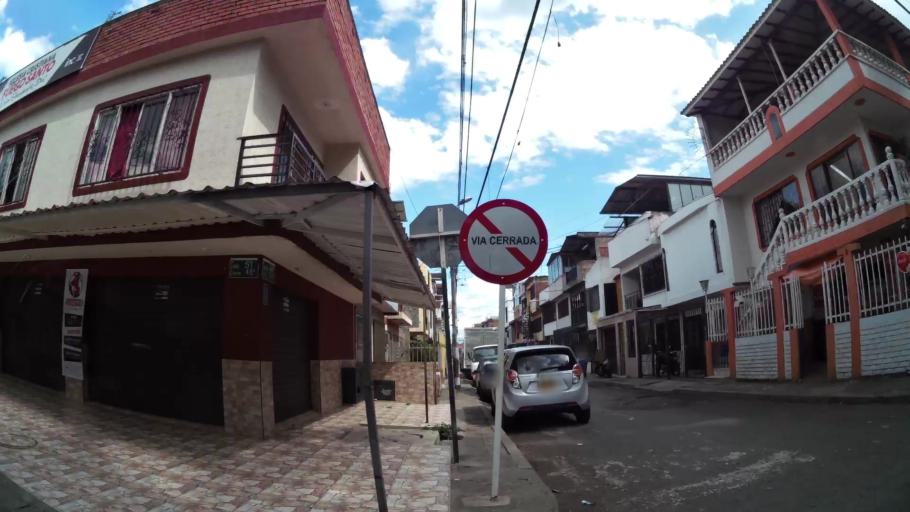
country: CO
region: Valle del Cauca
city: Cali
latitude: 3.3978
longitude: -76.5115
